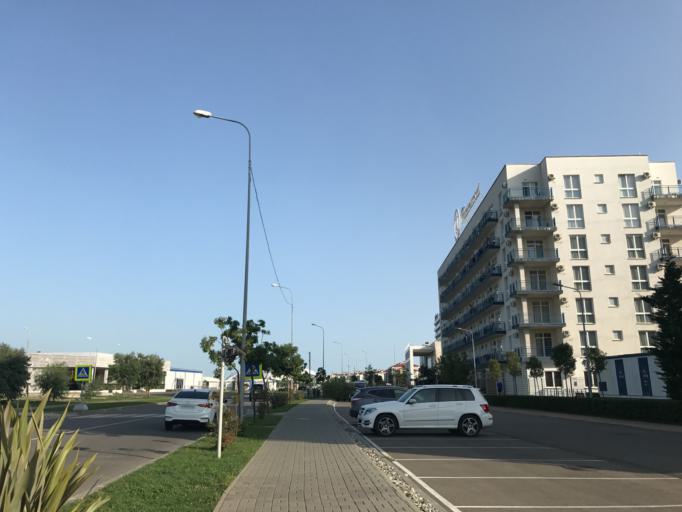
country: RU
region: Krasnodarskiy
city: Adler
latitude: 43.4122
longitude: 39.9363
